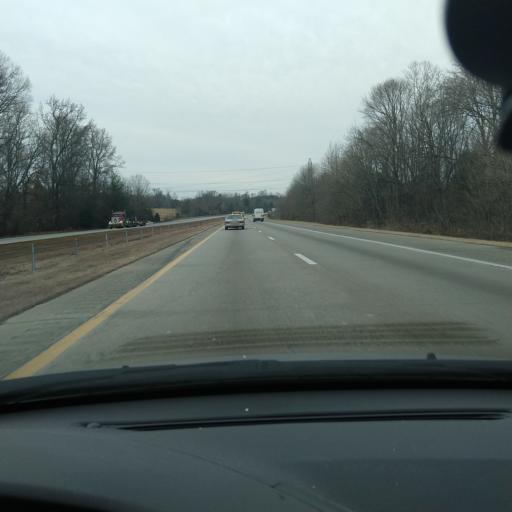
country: US
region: North Carolina
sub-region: Davidson County
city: Wallburg
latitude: 36.0707
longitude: -80.1541
